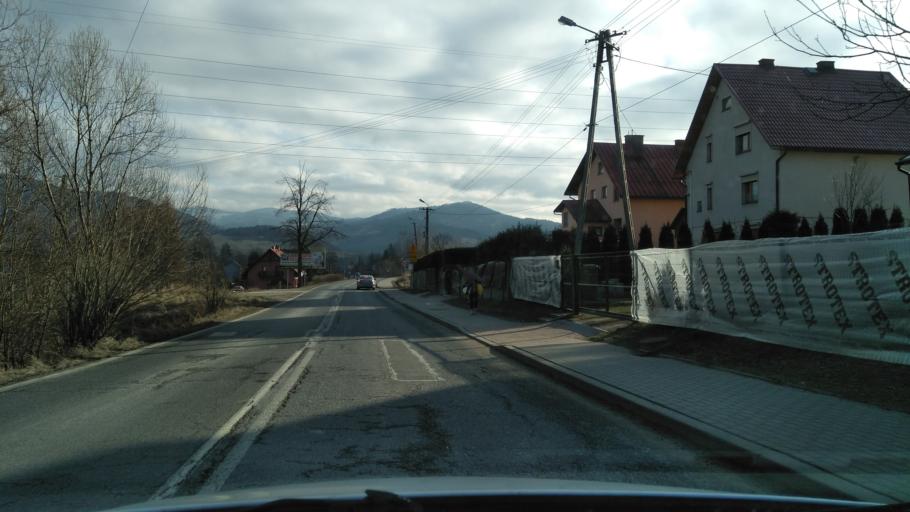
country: PL
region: Silesian Voivodeship
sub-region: Powiat zywiecki
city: Milowka
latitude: 49.5642
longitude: 19.0738
